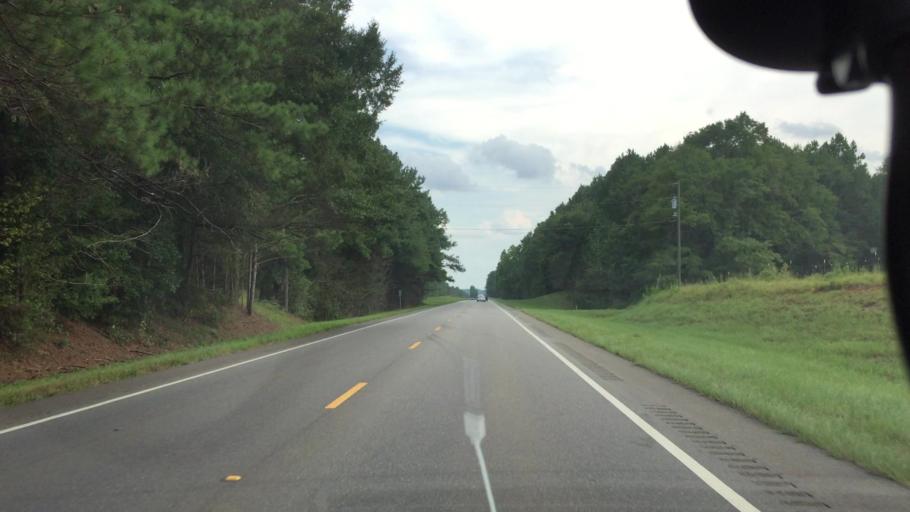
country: US
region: Alabama
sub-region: Coffee County
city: New Brockton
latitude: 31.5049
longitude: -85.9157
